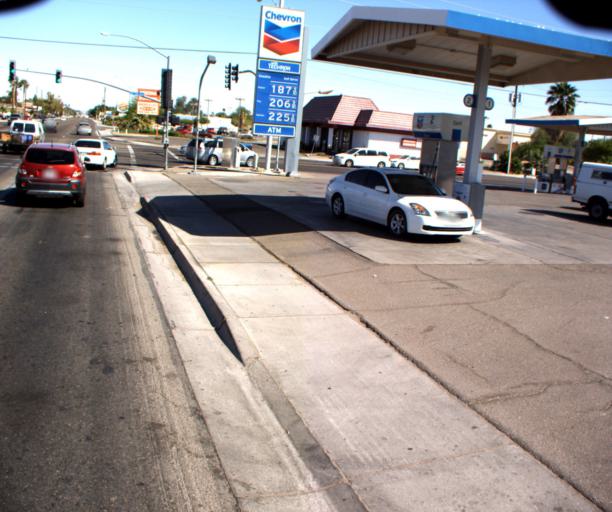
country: US
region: Arizona
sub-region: Yuma County
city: Yuma
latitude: 32.6980
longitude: -114.6503
